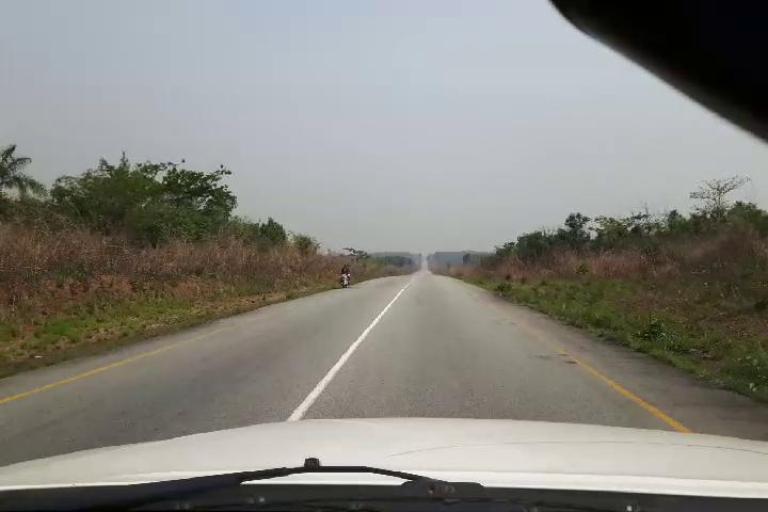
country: SL
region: Southern Province
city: Largo
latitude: 8.2401
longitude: -12.0848
